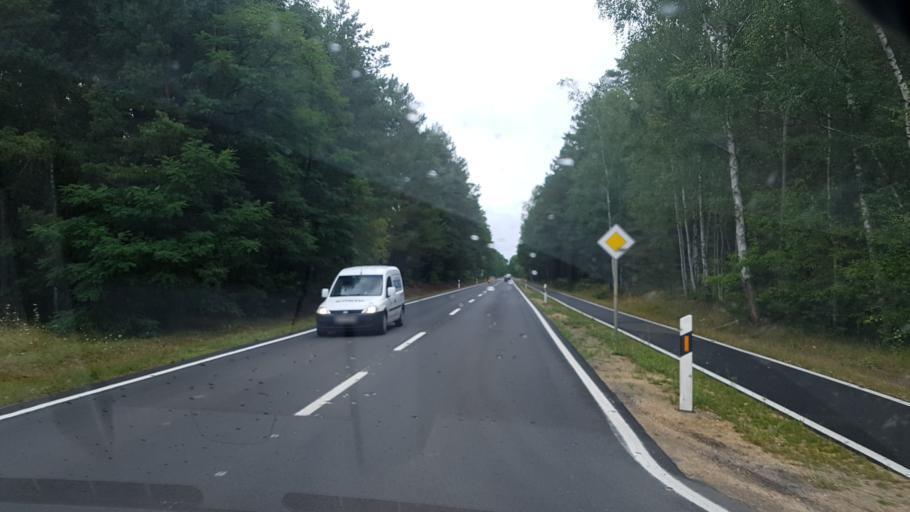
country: DE
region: Saxony
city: Niesky
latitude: 51.3067
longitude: 14.8155
